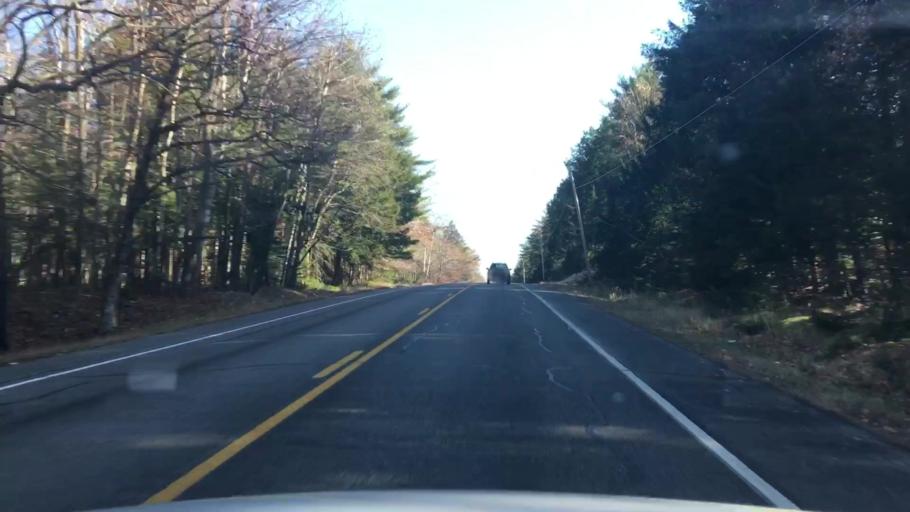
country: US
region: Maine
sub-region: Knox County
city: Washington
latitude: 44.2274
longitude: -69.3382
